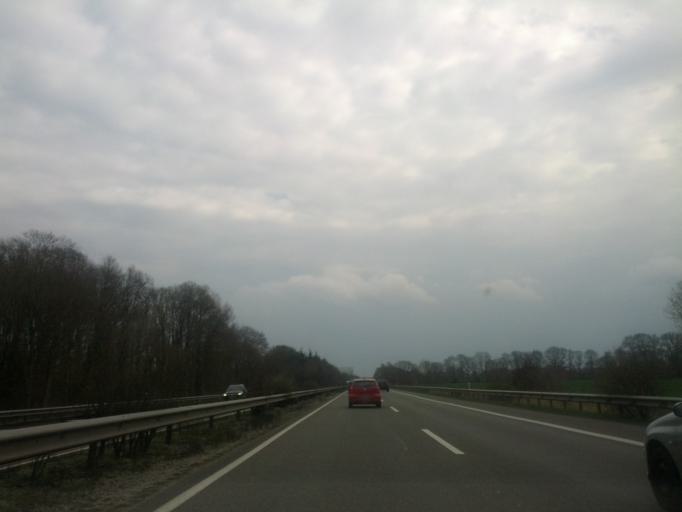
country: DE
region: Lower Saxony
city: Westerstede
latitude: 53.2745
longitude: 7.9161
